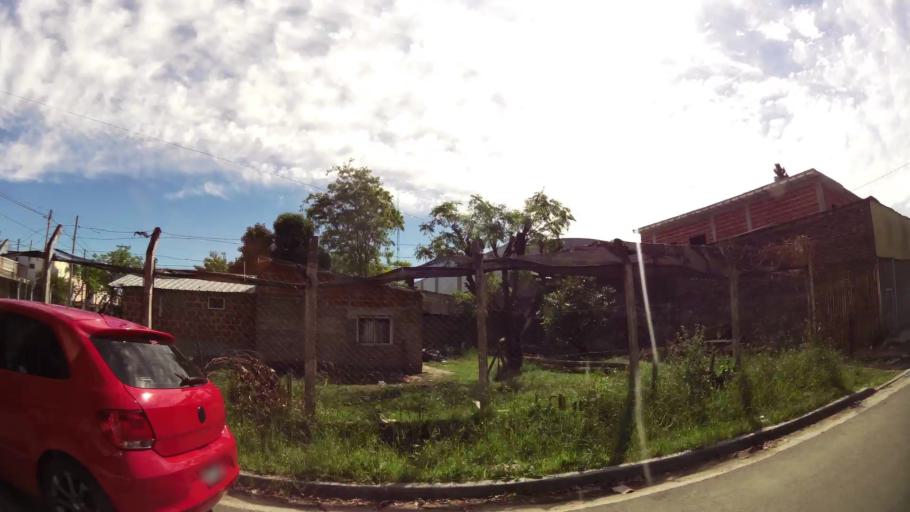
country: AR
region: Buenos Aires
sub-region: Partido de Quilmes
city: Quilmes
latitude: -34.7705
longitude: -58.2901
